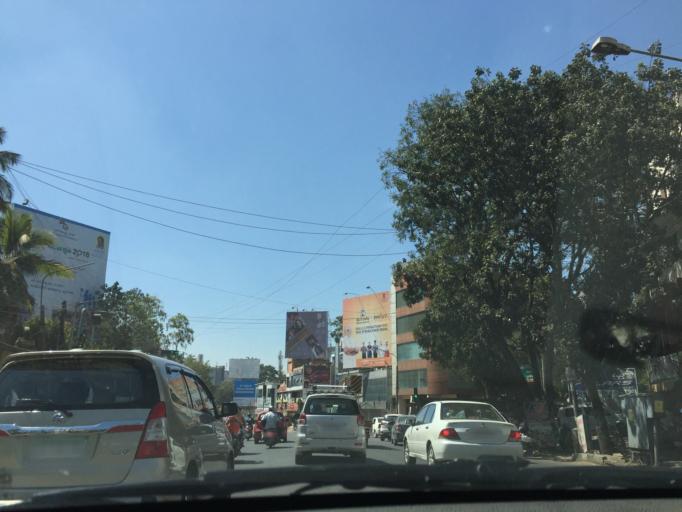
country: IN
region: Karnataka
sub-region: Bangalore Urban
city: Bangalore
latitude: 12.9613
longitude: 77.5886
